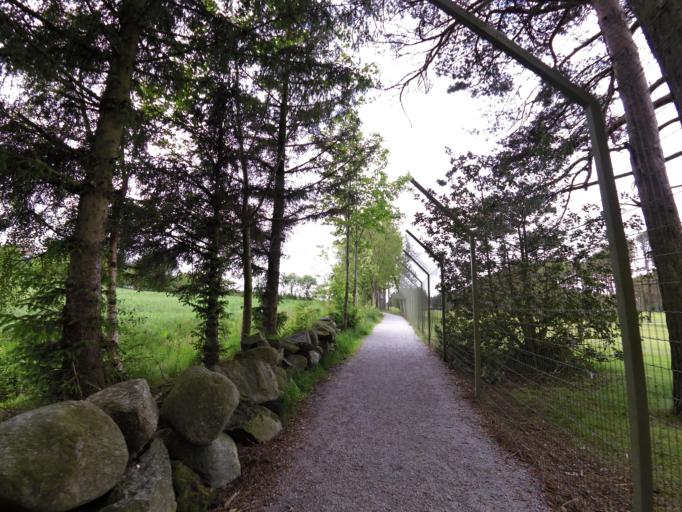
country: NO
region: Rogaland
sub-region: Randaberg
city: Randaberg
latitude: 58.9570
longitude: 5.6630
